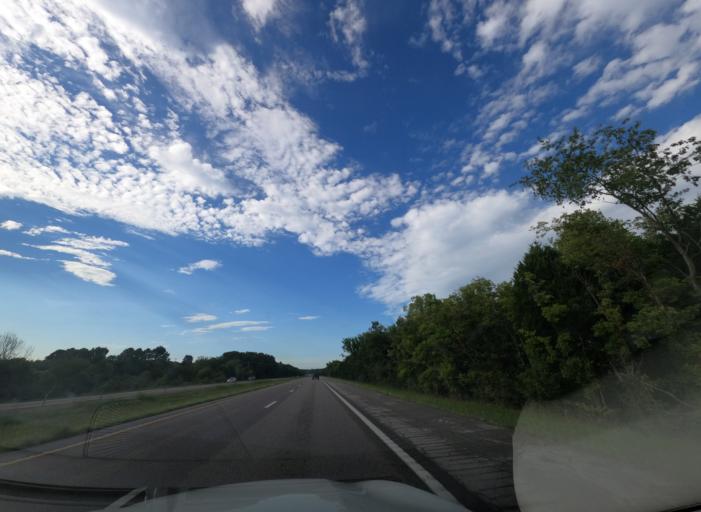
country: US
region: Missouri
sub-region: Jefferson County
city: Crystal City
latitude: 38.1145
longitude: -90.3078
